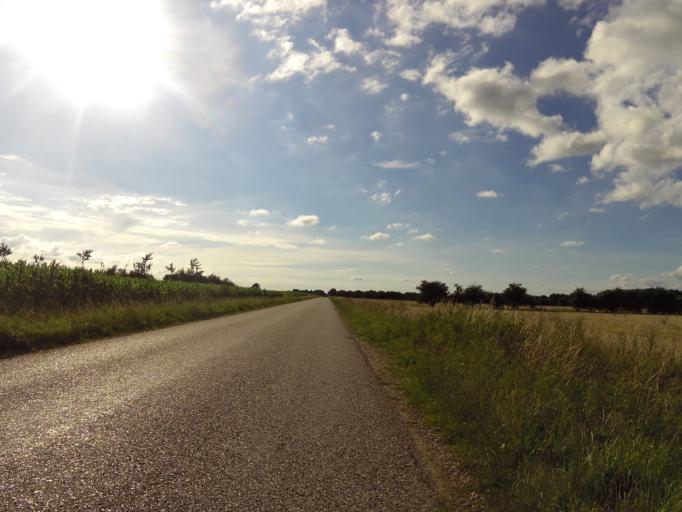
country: DK
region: South Denmark
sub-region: Haderslev Kommune
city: Vojens
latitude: 55.2012
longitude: 9.2908
